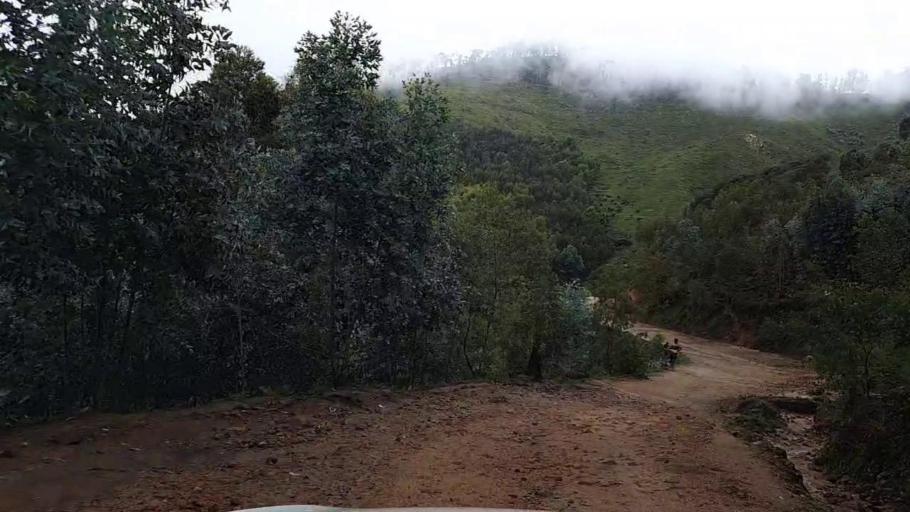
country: RW
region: Southern Province
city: Nzega
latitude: -2.3941
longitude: 29.4975
